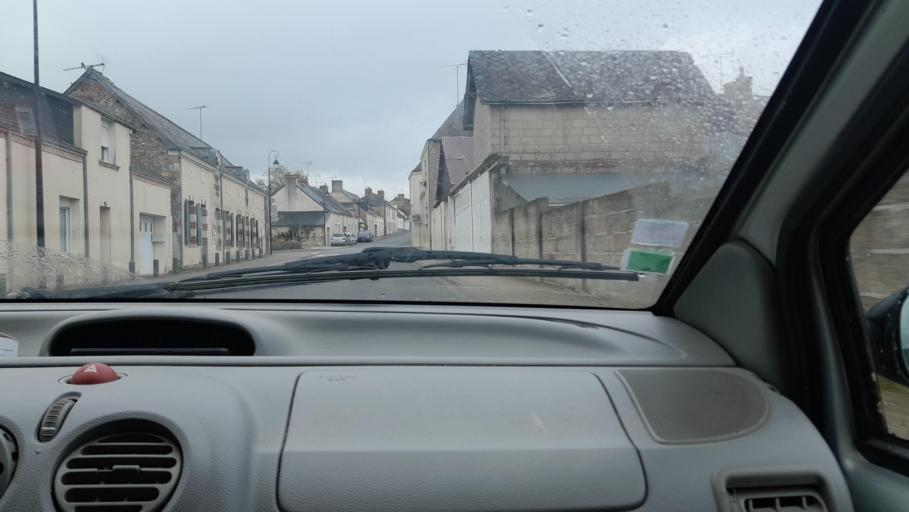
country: FR
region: Pays de la Loire
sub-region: Departement de la Mayenne
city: Congrier
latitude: 47.8393
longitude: -1.1386
